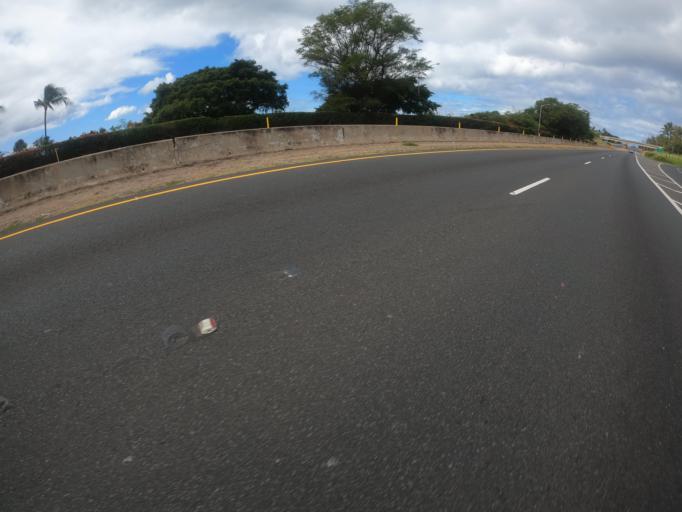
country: US
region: Hawaii
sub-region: Honolulu County
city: Makakilo City
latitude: 21.3448
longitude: -158.1207
